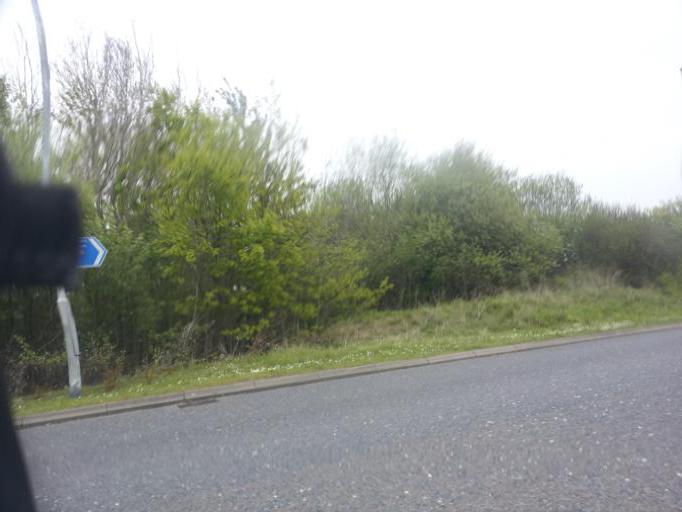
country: GB
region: England
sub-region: Medway
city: High Halstow
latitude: 51.4440
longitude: 0.5798
